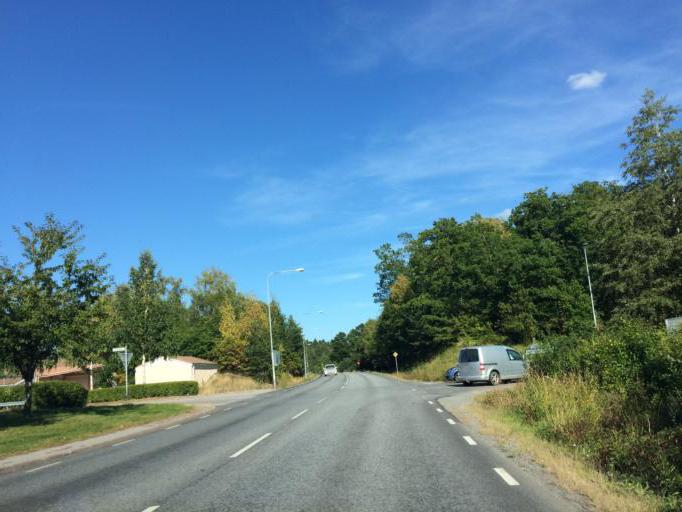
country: SE
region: Stockholm
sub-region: Upplands Vasby Kommun
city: Upplands Vaesby
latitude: 59.4846
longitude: 17.9281
